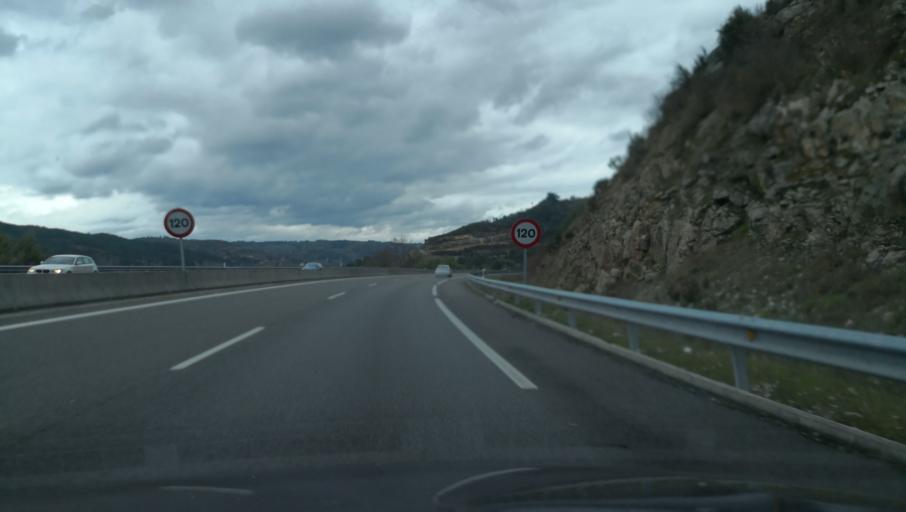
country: ES
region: Galicia
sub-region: Provincia de Ourense
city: Punxin
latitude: 42.3540
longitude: -7.9990
